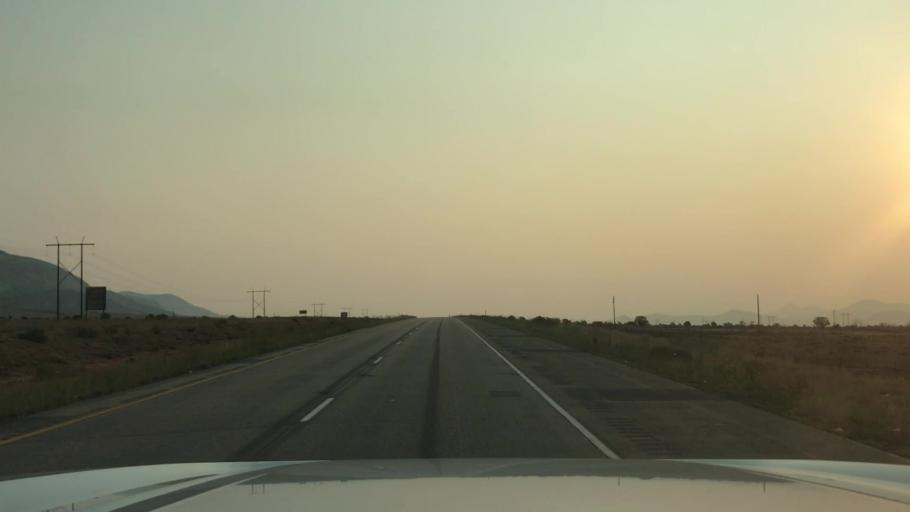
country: US
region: Utah
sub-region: Sevier County
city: Richfield
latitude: 38.8042
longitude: -112.0641
